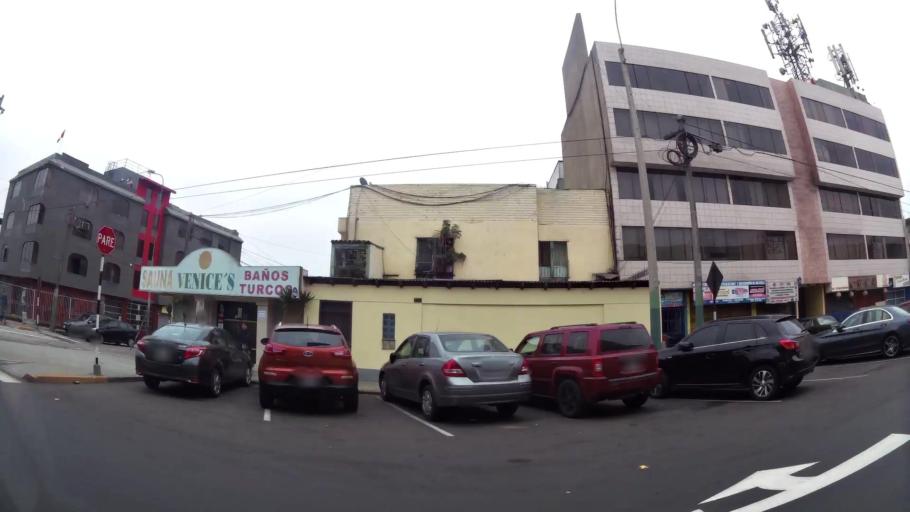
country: PE
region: Lima
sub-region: Lima
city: San Luis
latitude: -12.1018
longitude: -77.0017
